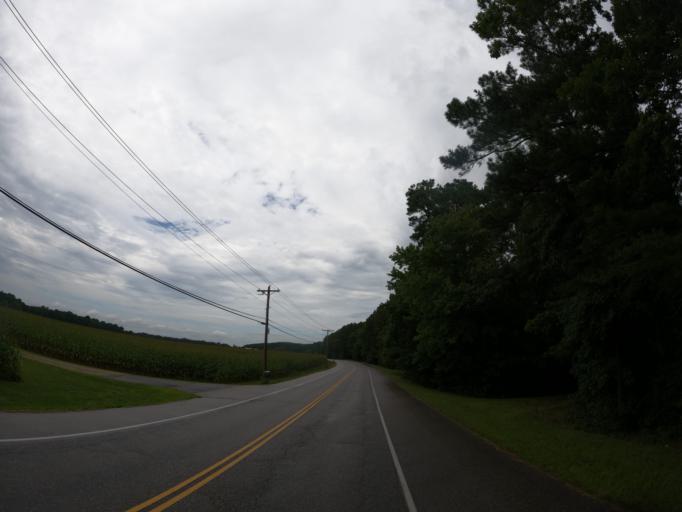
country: US
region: Maryland
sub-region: Saint Mary's County
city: California
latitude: 38.2646
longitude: -76.5267
